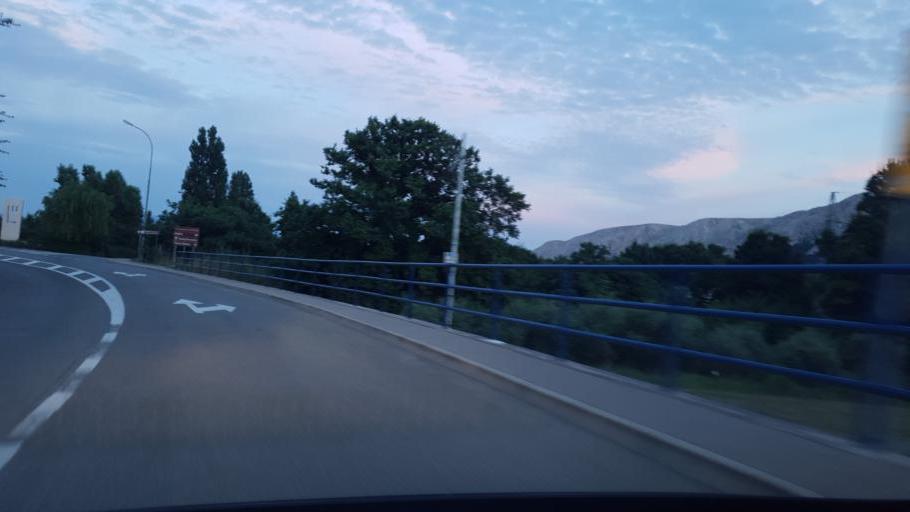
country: HR
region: Primorsko-Goranska
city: Punat
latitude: 44.9748
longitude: 14.7386
